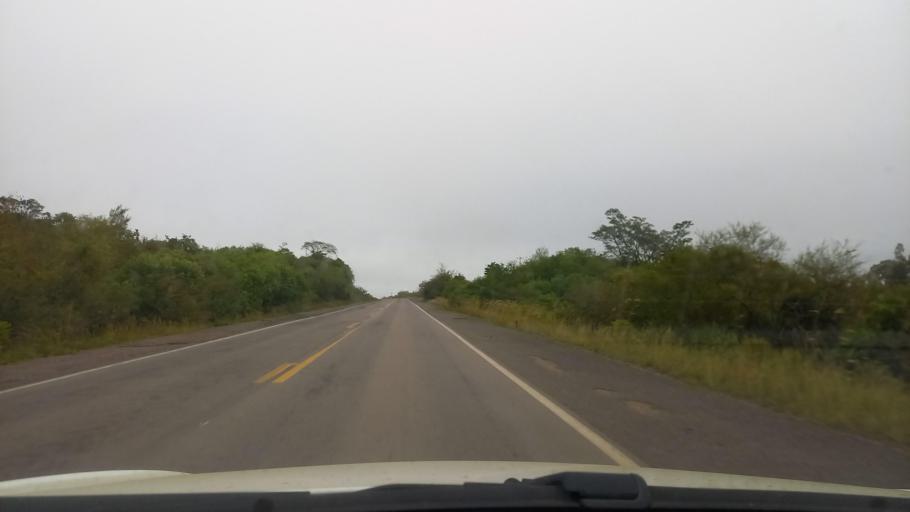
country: BR
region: Rio Grande do Sul
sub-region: Cacequi
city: Cacequi
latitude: -30.1237
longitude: -54.6477
